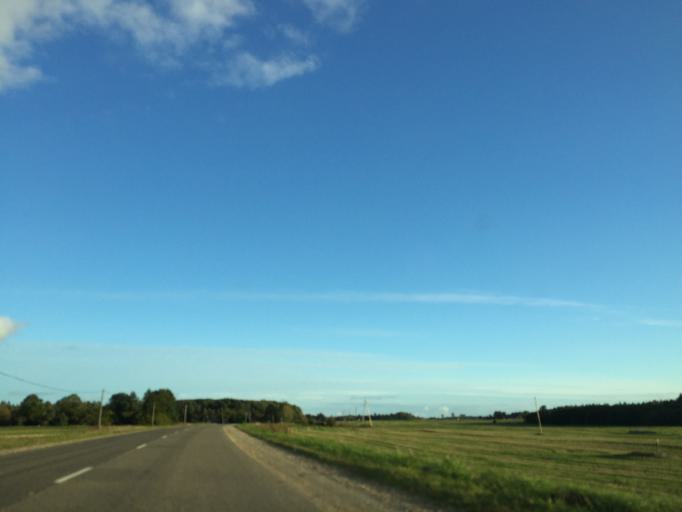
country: LV
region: Saldus Rajons
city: Saldus
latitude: 56.7467
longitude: 22.3766
